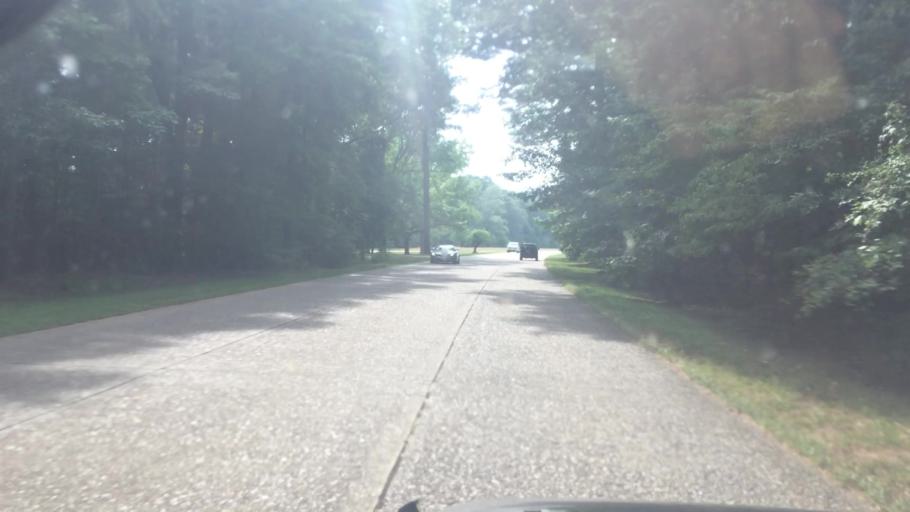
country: US
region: Virginia
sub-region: James City County
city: Williamsburg
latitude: 37.2168
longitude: -76.7555
